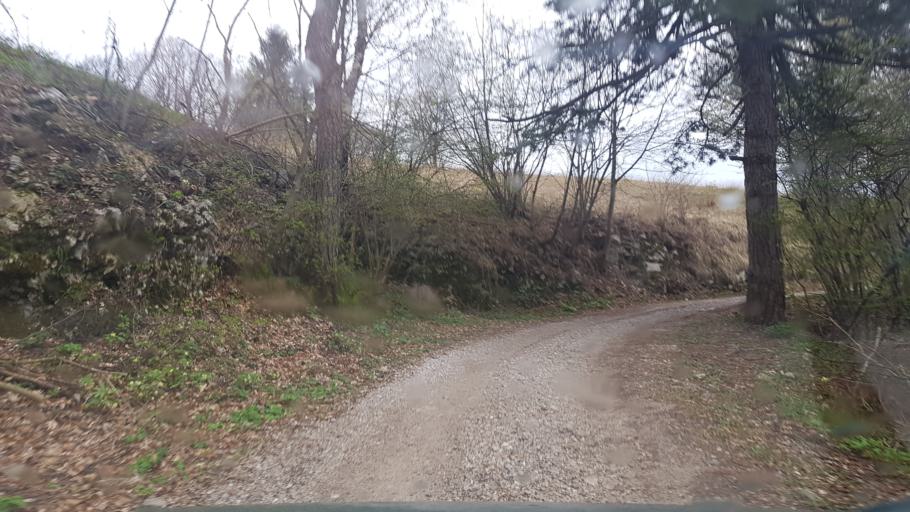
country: SI
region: Kanal
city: Deskle
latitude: 46.0666
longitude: 13.5635
